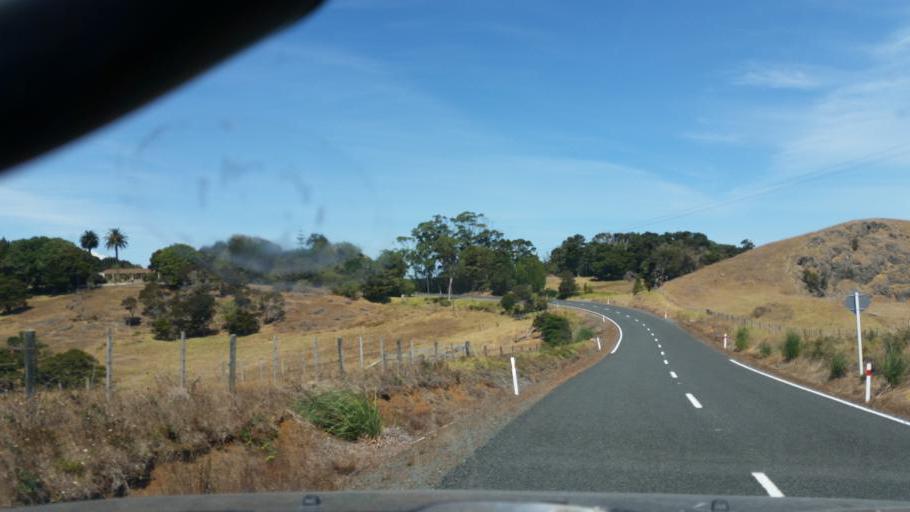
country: NZ
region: Auckland
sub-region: Auckland
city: Wellsford
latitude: -36.2260
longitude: 174.2097
